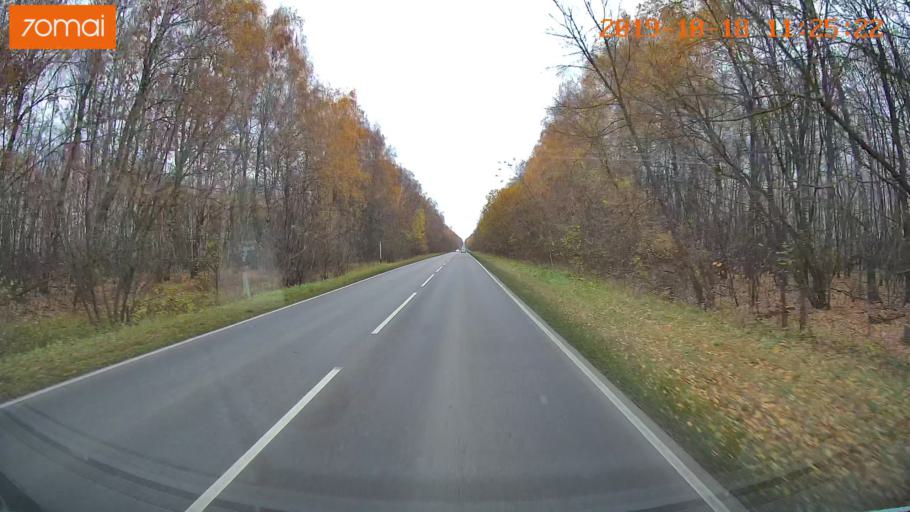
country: RU
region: Tula
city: Kimovsk
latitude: 54.1234
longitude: 38.6167
